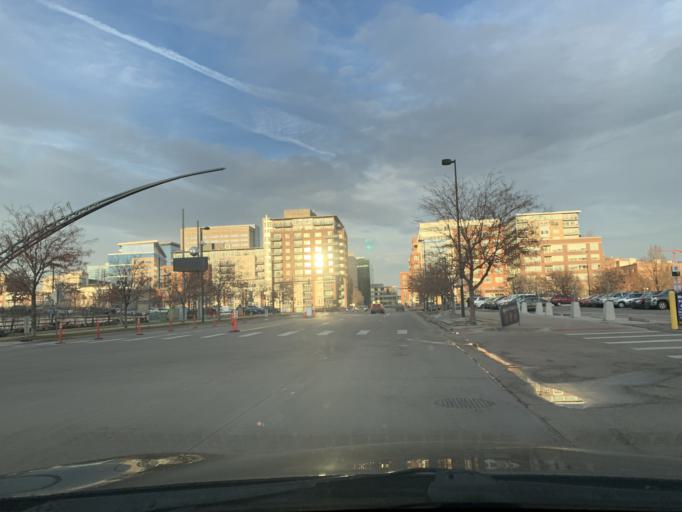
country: US
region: Colorado
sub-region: Denver County
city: Denver
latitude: 39.7493
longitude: -105.0058
